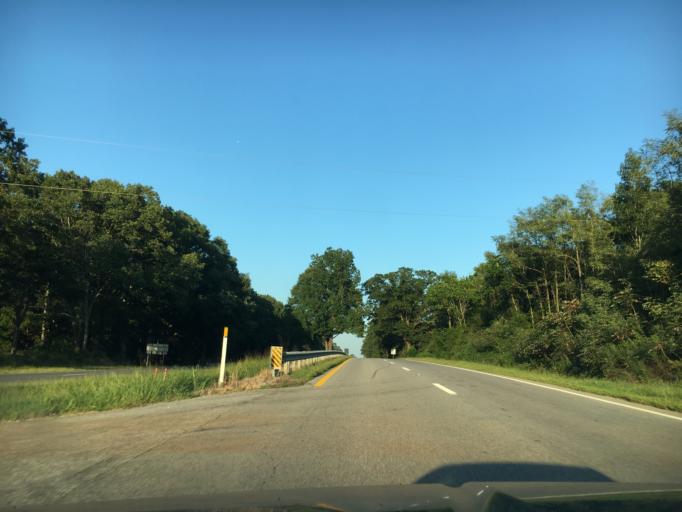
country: US
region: Virginia
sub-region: Halifax County
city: Mountain Road
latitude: 36.5847
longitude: -79.1376
